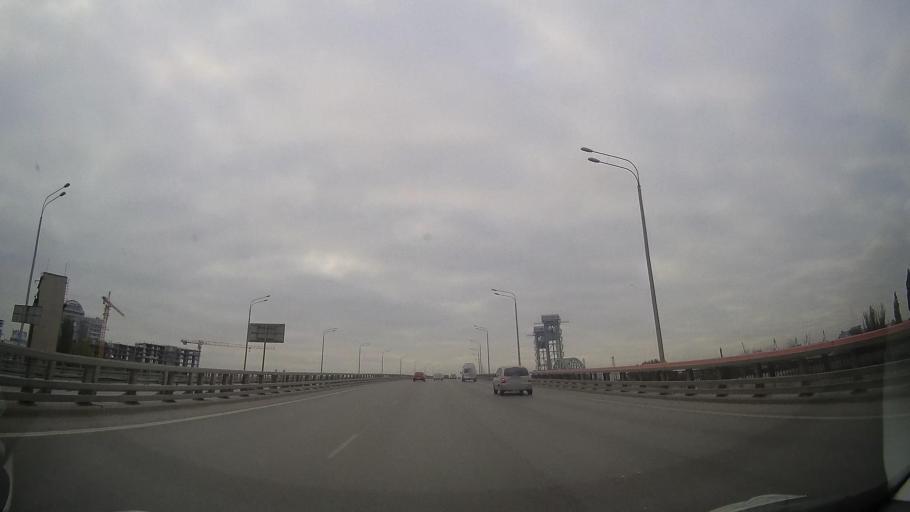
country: RU
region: Rostov
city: Rostov-na-Donu
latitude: 47.2133
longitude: 39.6999
